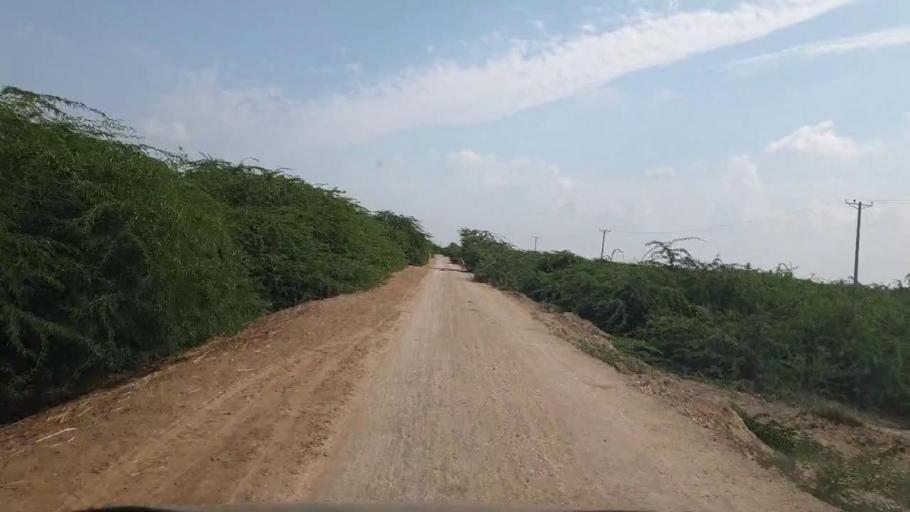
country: PK
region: Sindh
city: Badin
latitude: 24.4778
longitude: 68.6197
